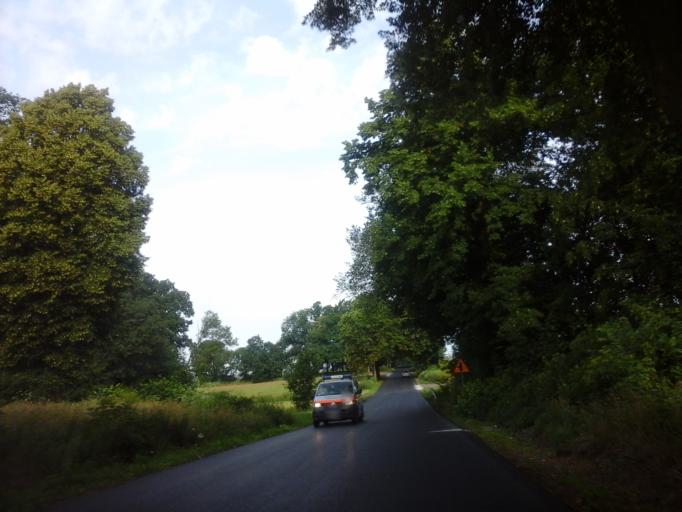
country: PL
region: West Pomeranian Voivodeship
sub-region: Powiat stargardzki
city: Stargard Szczecinski
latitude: 53.2715
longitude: 15.1300
